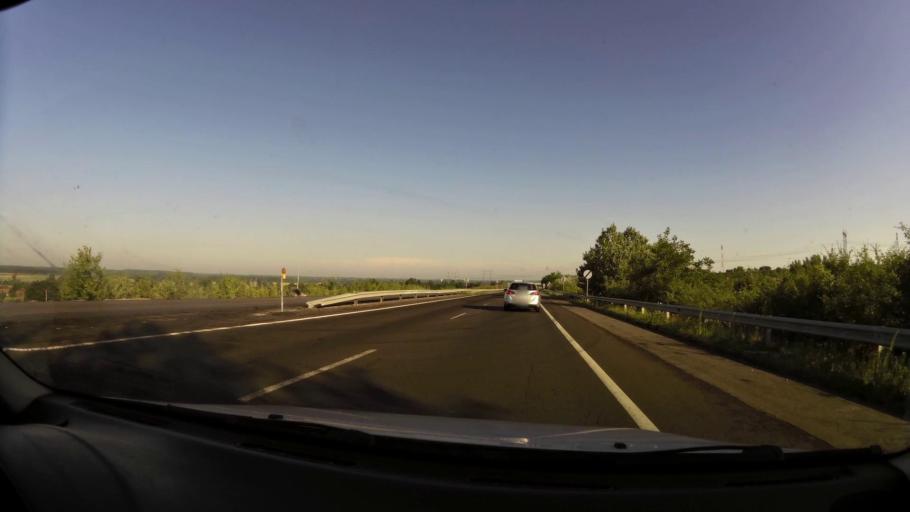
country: HU
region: Pest
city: Cegledbercel
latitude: 47.2313
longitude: 19.6732
